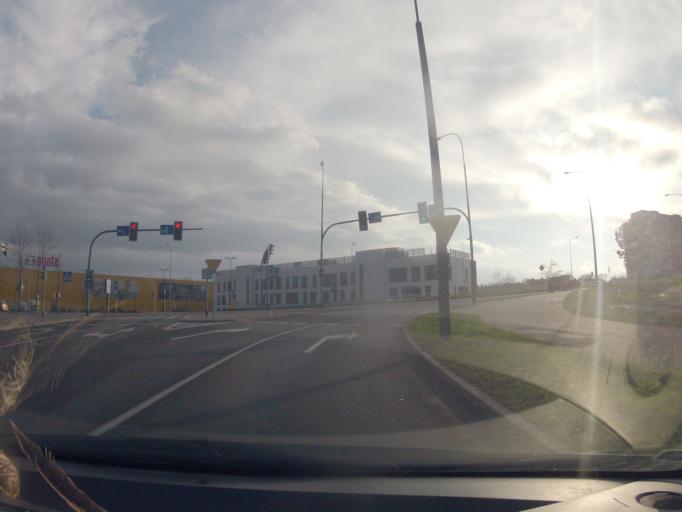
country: PL
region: Opole Voivodeship
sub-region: Powiat opolski
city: Opole
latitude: 50.6691
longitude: 17.9506
